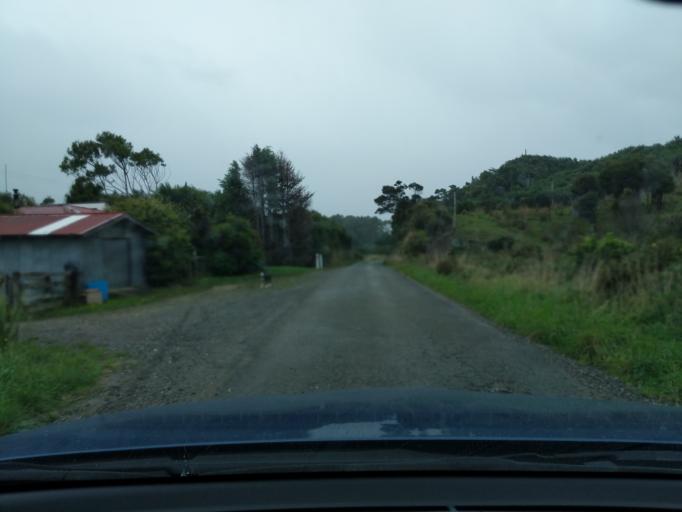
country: NZ
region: Tasman
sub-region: Tasman District
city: Takaka
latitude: -40.6355
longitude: 172.4895
